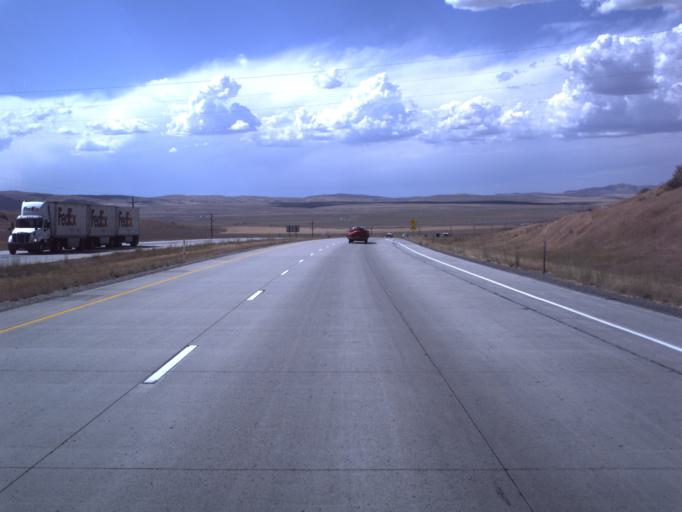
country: US
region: Utah
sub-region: Box Elder County
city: Garland
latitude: 41.8205
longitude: -112.4175
